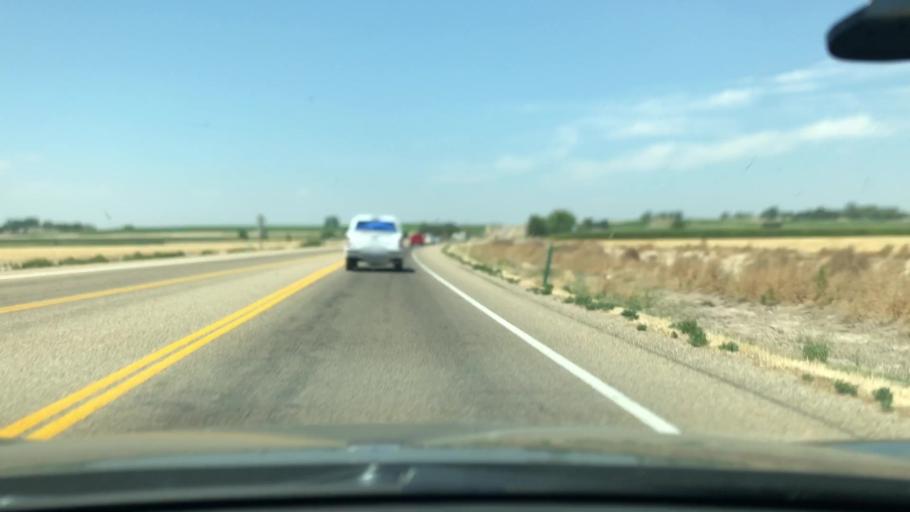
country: US
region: Idaho
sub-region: Canyon County
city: Parma
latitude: 43.8087
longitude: -116.9540
